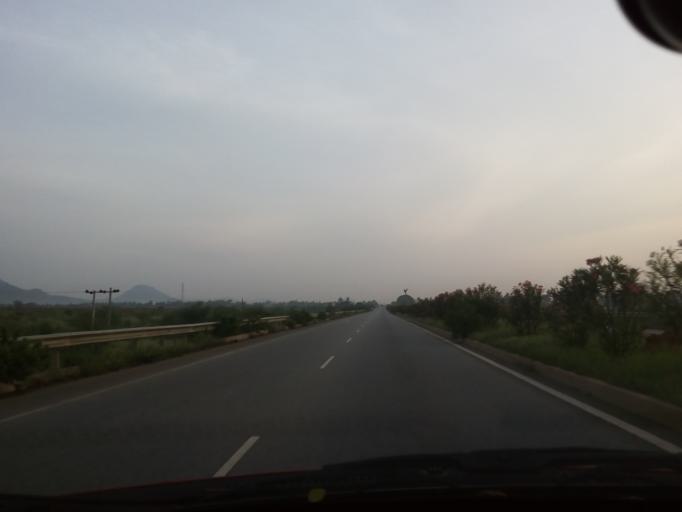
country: IN
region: Karnataka
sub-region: Bangalore Rural
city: Devanhalli
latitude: 13.3194
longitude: 77.7255
